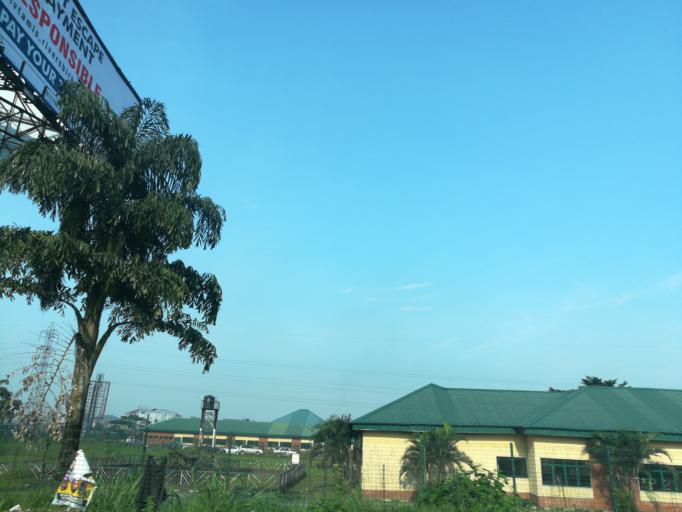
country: NG
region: Rivers
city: Port Harcourt
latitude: 4.8227
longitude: 7.0242
